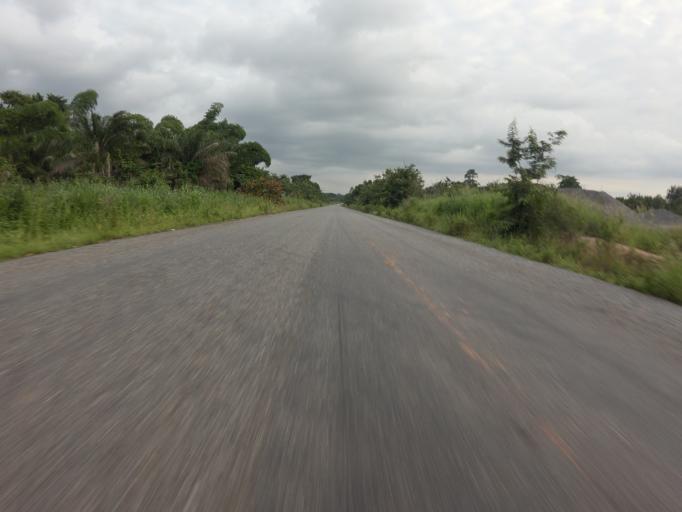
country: GH
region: Volta
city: Kpandu
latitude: 6.8351
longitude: 0.3825
